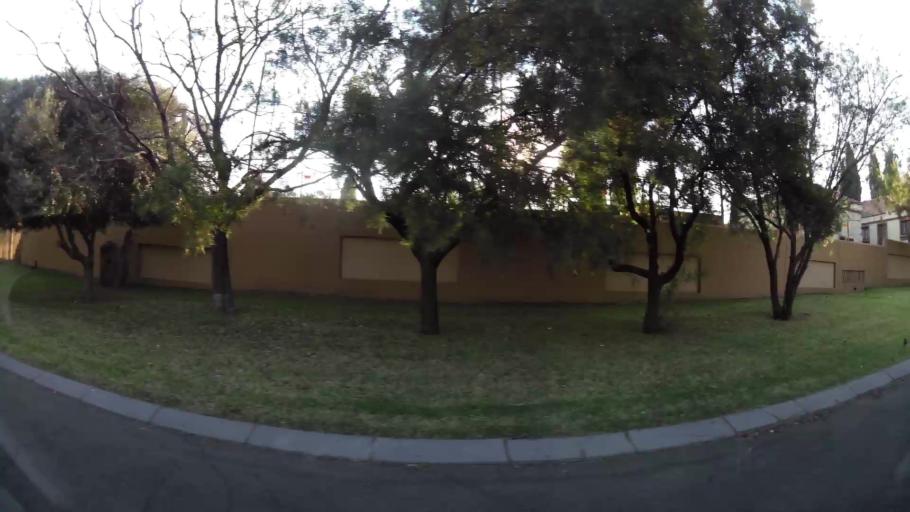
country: ZA
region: Gauteng
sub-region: City of Johannesburg Metropolitan Municipality
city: Modderfontein
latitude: -26.0725
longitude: 28.2235
